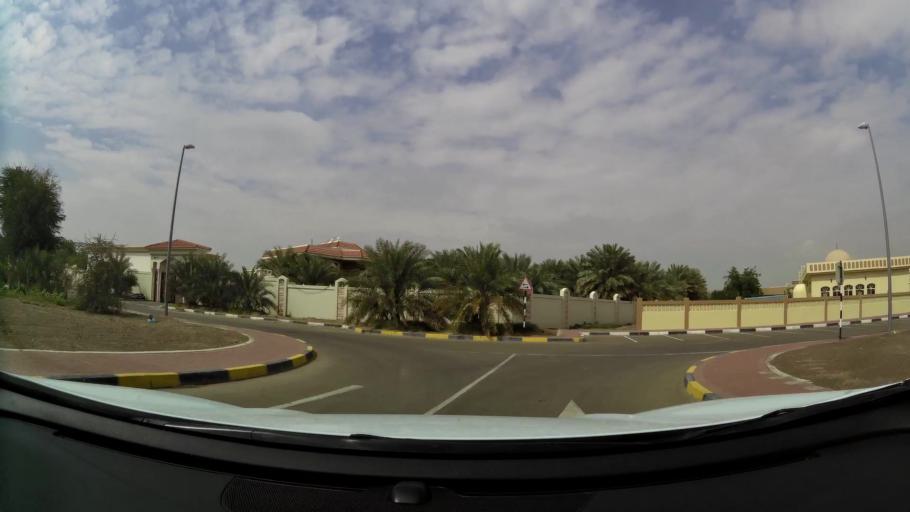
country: AE
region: Abu Dhabi
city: Al Ain
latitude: 24.1983
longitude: 55.8006
